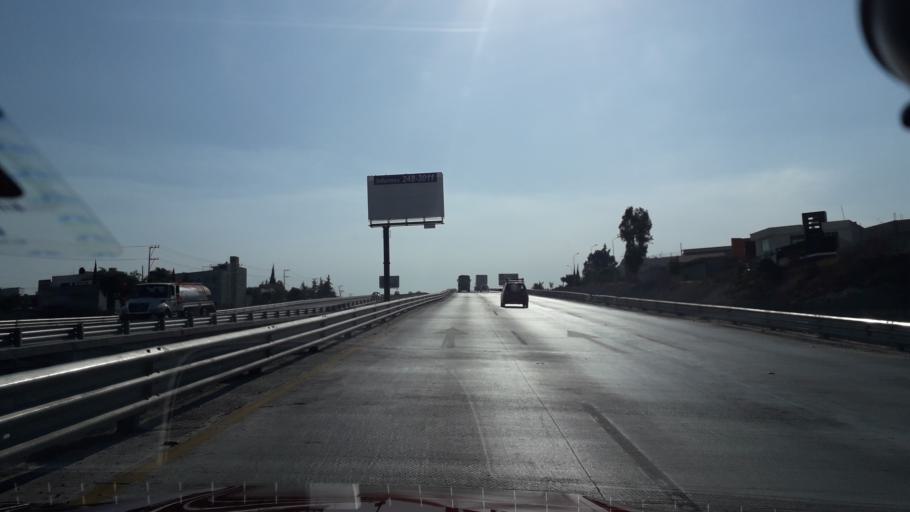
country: MX
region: Puebla
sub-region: Puebla
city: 18 de Marzo
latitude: 18.9720
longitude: -98.1941
